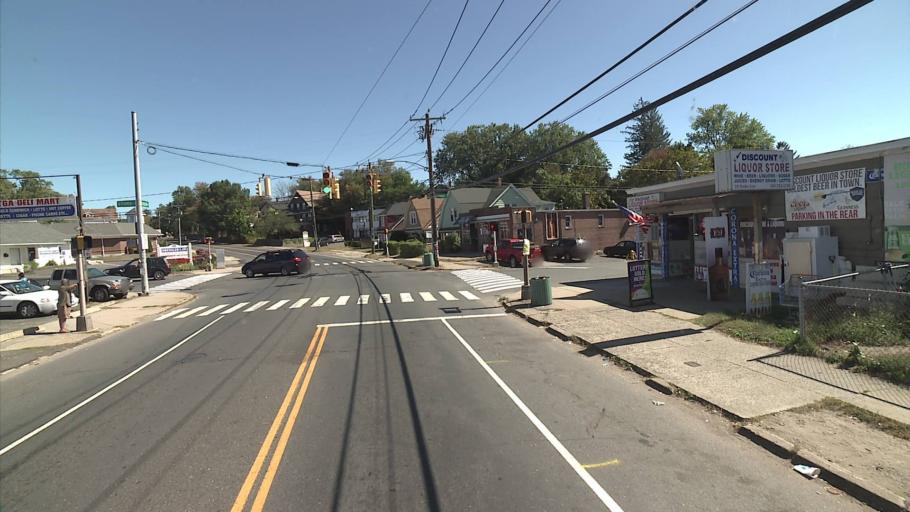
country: US
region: Connecticut
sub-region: New Haven County
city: Waterbury
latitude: 41.5503
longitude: -73.0105
